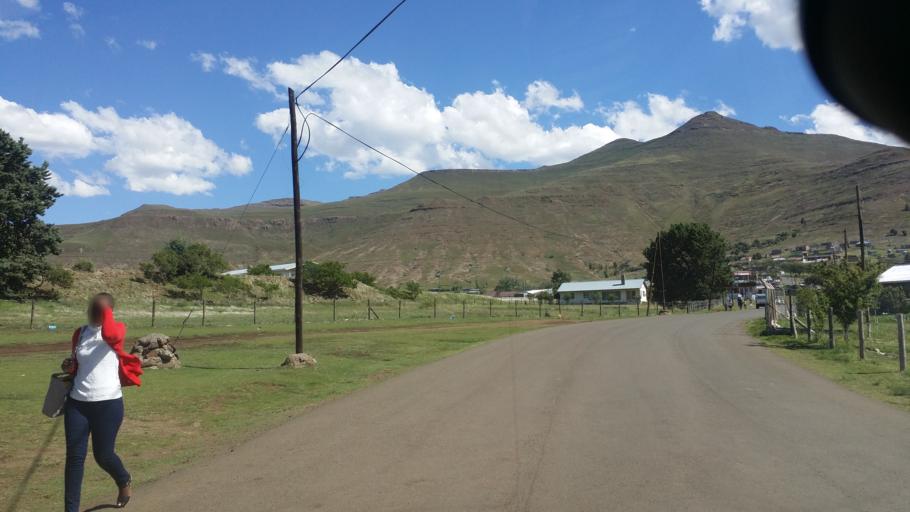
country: LS
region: Mokhotlong
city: Mokhotlong
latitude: -29.2843
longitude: 29.0697
